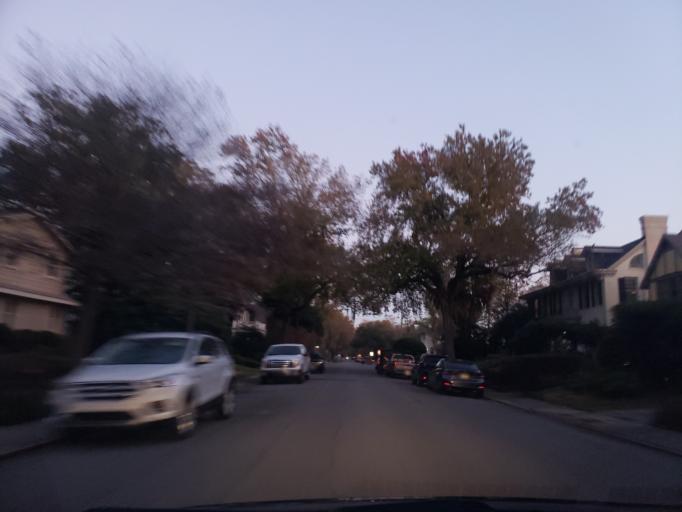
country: US
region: Georgia
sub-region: Chatham County
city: Savannah
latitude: 32.0498
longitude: -81.0948
